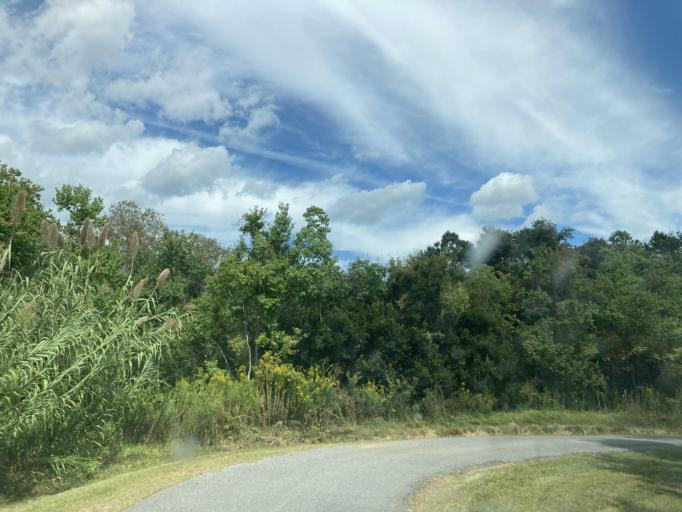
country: US
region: Mississippi
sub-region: Harrison County
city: D'Iberville
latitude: 30.4272
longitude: -88.8778
